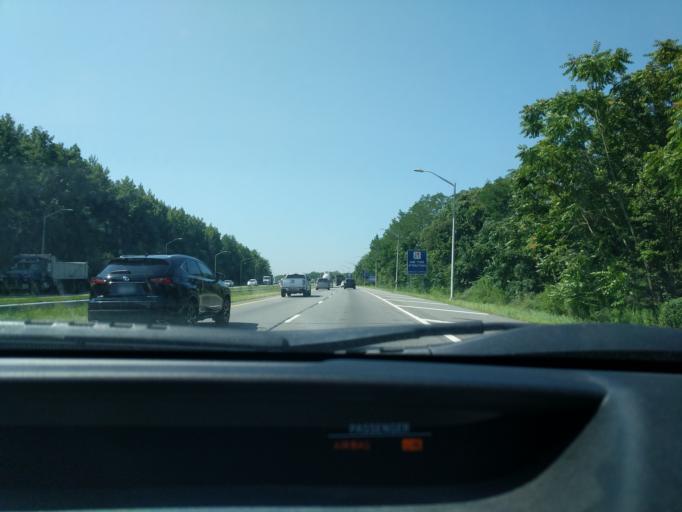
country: US
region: New Jersey
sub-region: Middlesex County
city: Carteret
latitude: 40.5474
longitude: -74.2216
